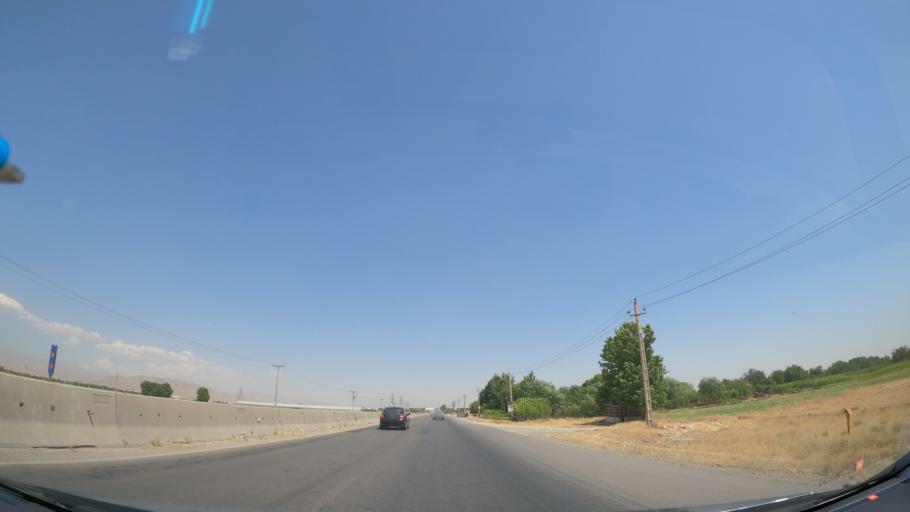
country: IR
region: Alborz
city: Hashtgerd
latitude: 35.9268
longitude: 50.7351
